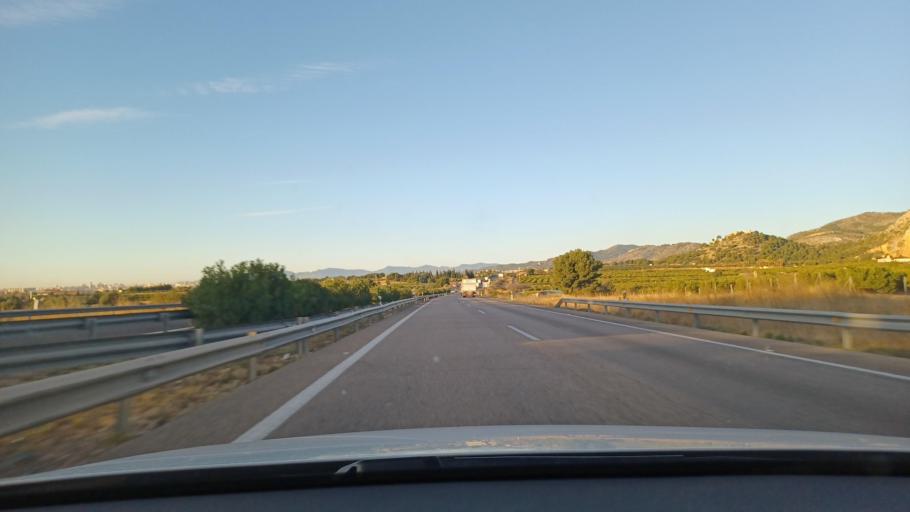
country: ES
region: Valencia
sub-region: Provincia de Castello
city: Benicassim
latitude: 40.0358
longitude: 0.0114
